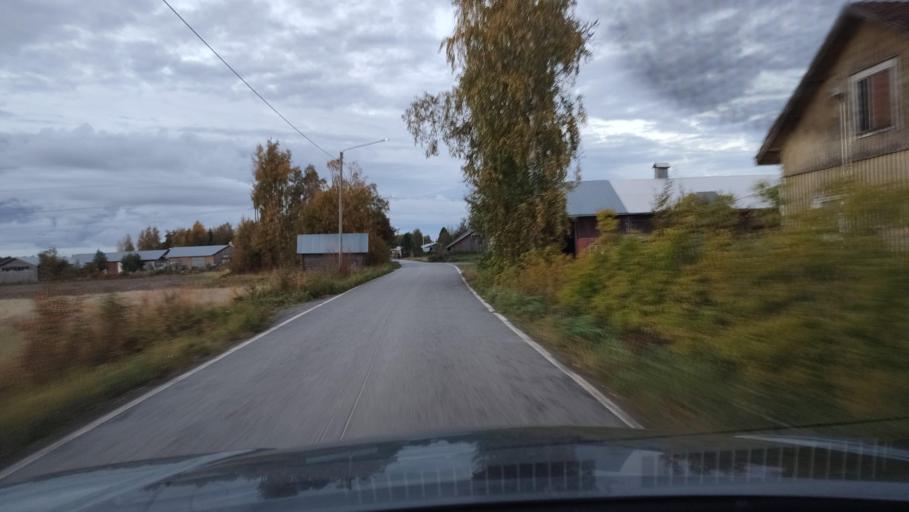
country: FI
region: Ostrobothnia
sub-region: Sydosterbotten
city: Kristinestad
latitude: 62.2681
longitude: 21.5092
